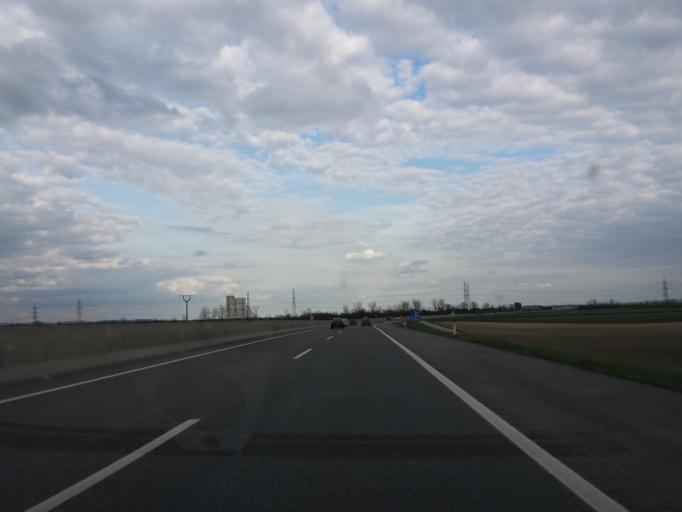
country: AT
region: Lower Austria
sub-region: Politischer Bezirk Tulln
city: Kirchberg am Wagram
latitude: 48.4100
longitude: 15.8653
